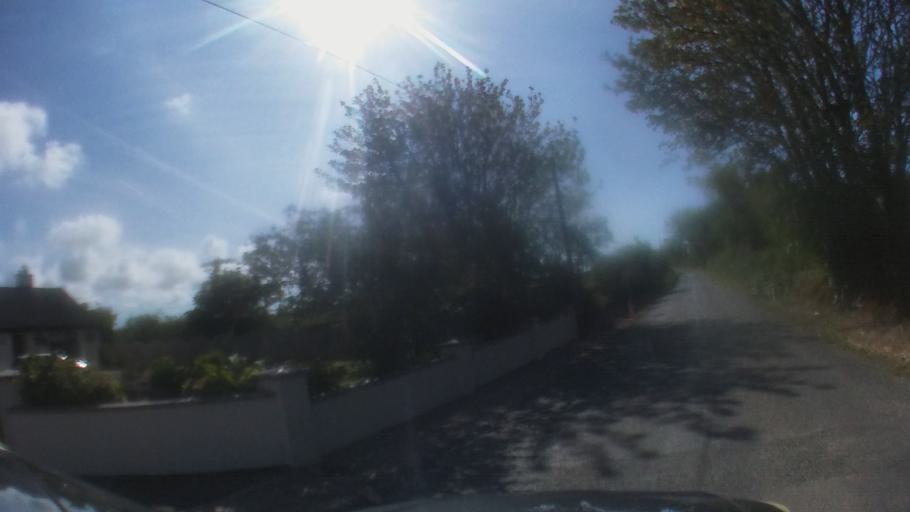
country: IE
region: Leinster
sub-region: Loch Garman
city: Loch Garman
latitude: 52.2269
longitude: -6.5486
